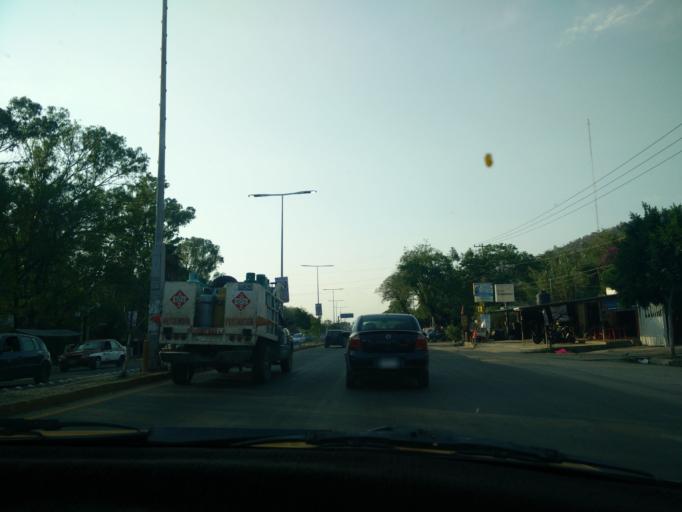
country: MX
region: Oaxaca
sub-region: Santa Maria Atzompa
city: San Jeronimo Yahuiche
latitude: 17.1014
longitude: -96.7516
